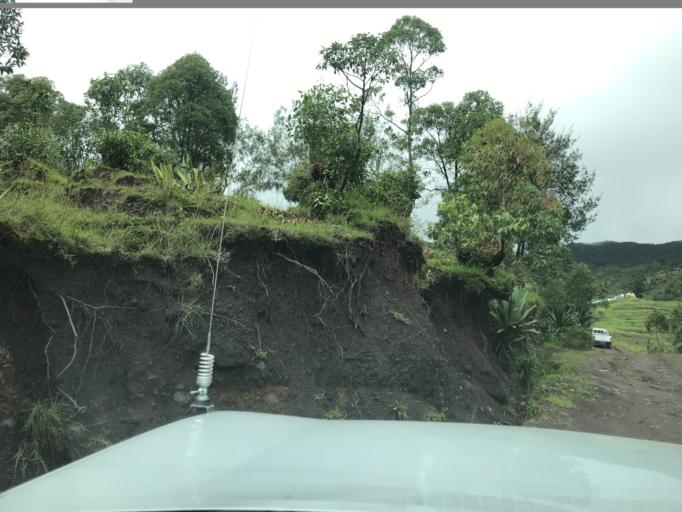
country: TL
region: Ainaro
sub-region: Ainaro
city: Ainaro
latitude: -8.8653
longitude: 125.5558
